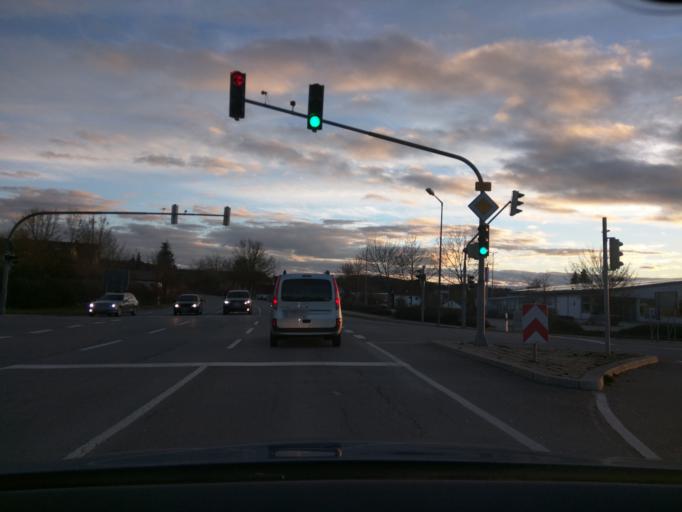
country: DE
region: Bavaria
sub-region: Upper Bavaria
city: Zolling
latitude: 48.4519
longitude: 11.7654
